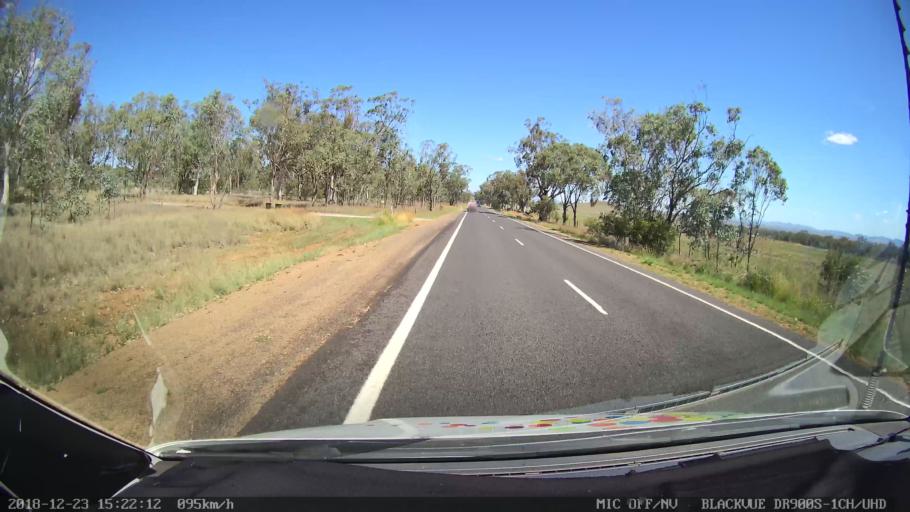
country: AU
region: New South Wales
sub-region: Tamworth Municipality
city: Manilla
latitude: -30.8654
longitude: 150.8027
